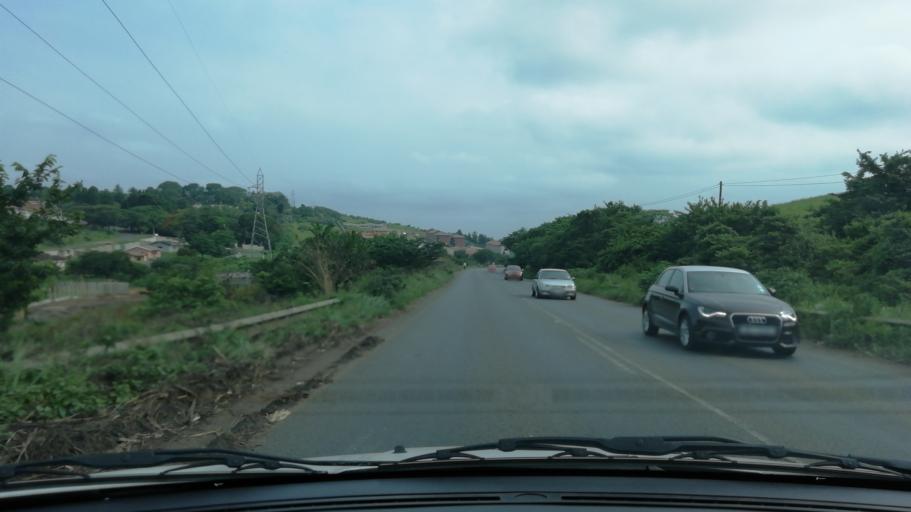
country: ZA
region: KwaZulu-Natal
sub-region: uThungulu District Municipality
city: Empangeni
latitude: -28.7459
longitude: 31.8807
